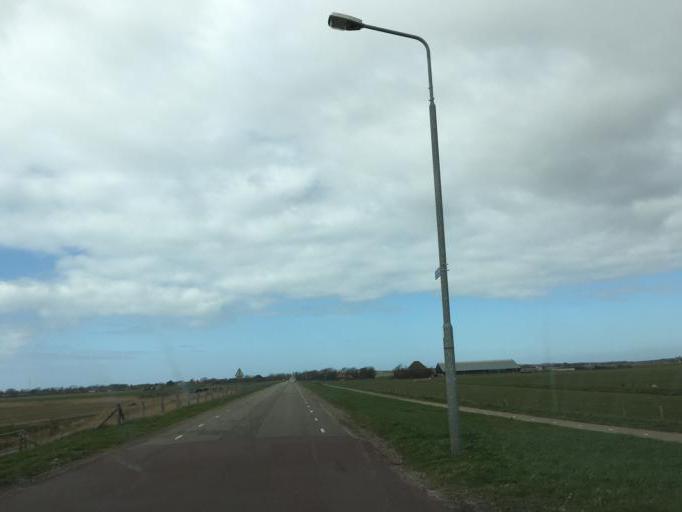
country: NL
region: North Holland
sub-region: Gemeente Schagen
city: Schagen
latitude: 52.8535
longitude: 4.7342
